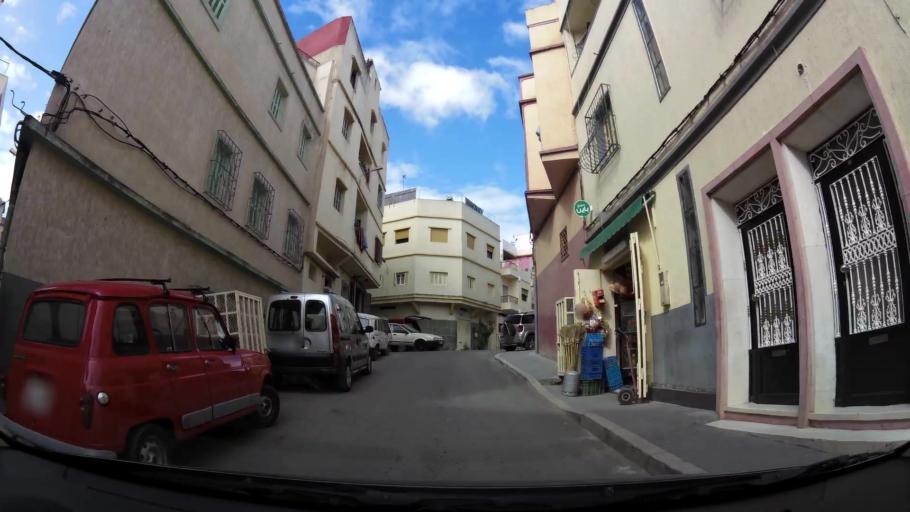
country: MA
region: Tanger-Tetouan
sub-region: Tanger-Assilah
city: Tangier
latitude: 35.7725
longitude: -5.8278
